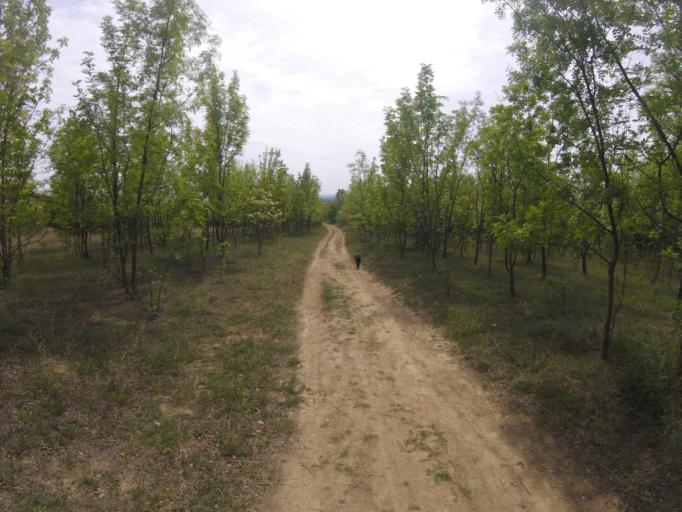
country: HU
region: Pest
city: Telki
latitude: 47.5559
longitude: 18.8326
